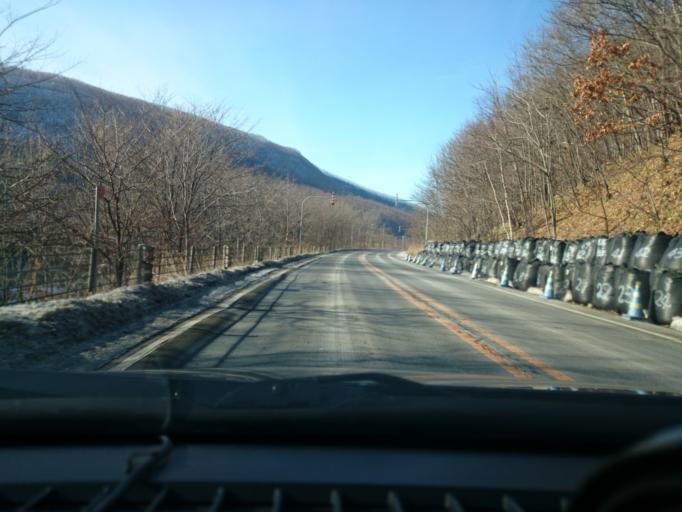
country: JP
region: Hokkaido
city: Otofuke
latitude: 43.2530
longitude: 143.4647
